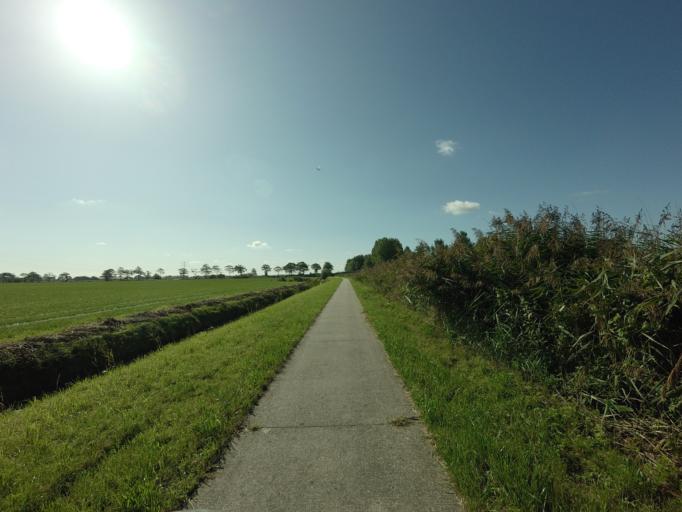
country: NL
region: Friesland
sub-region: Gemeente Leeuwarden
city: Wirdum
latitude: 53.1510
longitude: 5.7639
